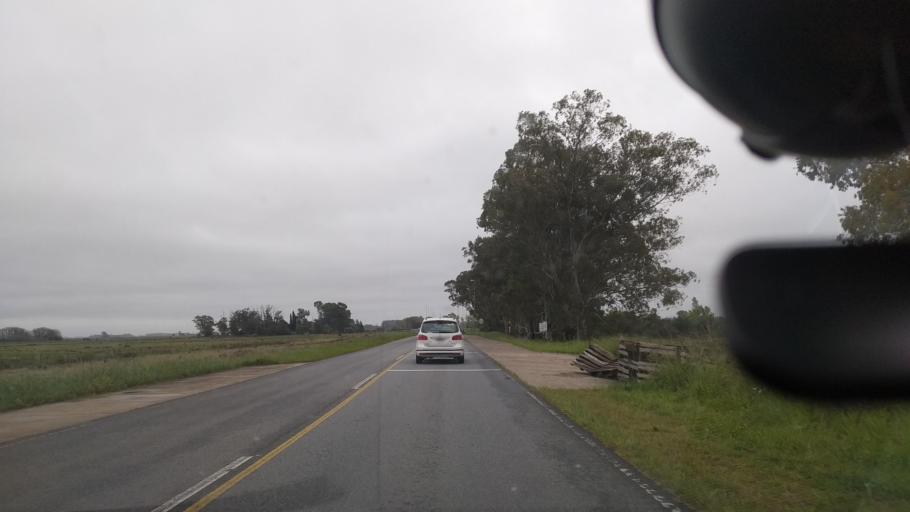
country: AR
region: Buenos Aires
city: Veronica
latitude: -35.3868
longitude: -57.3633
